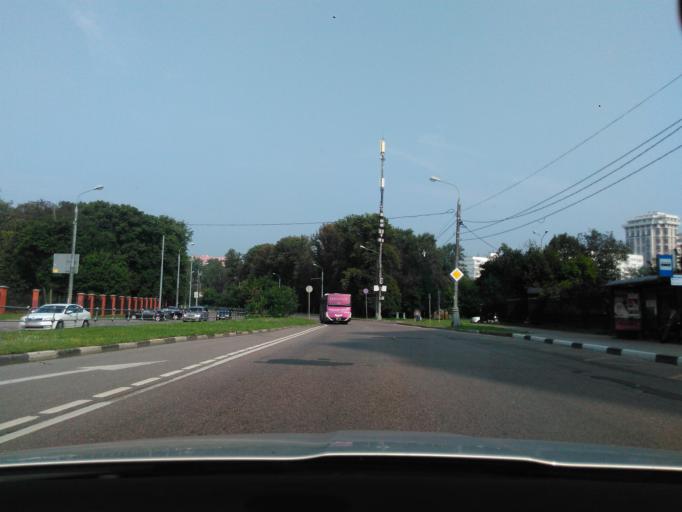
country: RU
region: Moscow
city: Sokol
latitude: 55.7928
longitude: 37.5233
